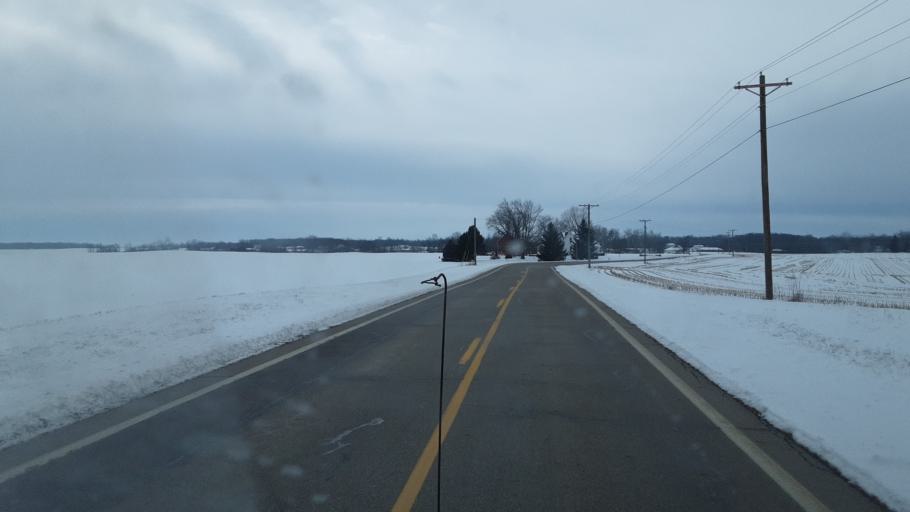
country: US
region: Ohio
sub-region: Champaign County
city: Mechanicsburg
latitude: 40.0464
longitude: -83.5329
